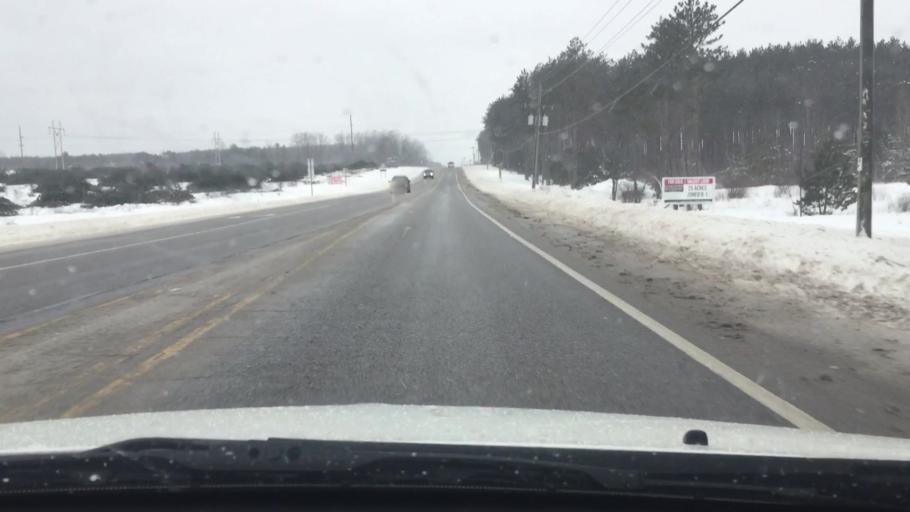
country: US
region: Michigan
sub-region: Otsego County
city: Gaylord
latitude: 45.0276
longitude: -84.7279
